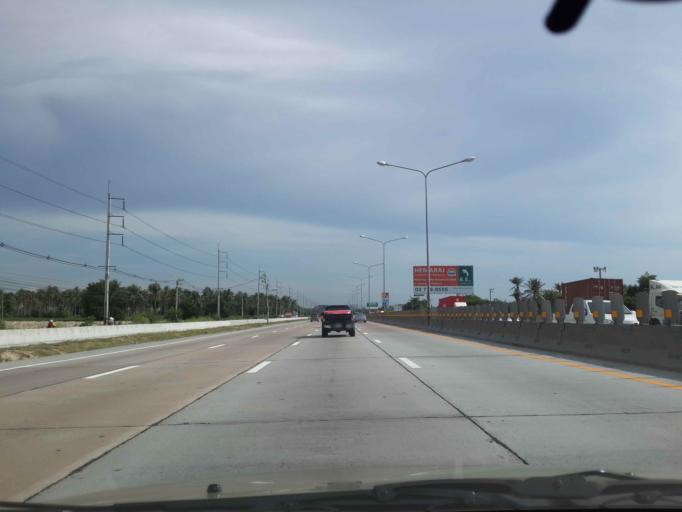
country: TH
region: Chon Buri
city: Si Racha
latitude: 13.1995
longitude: 101.0016
